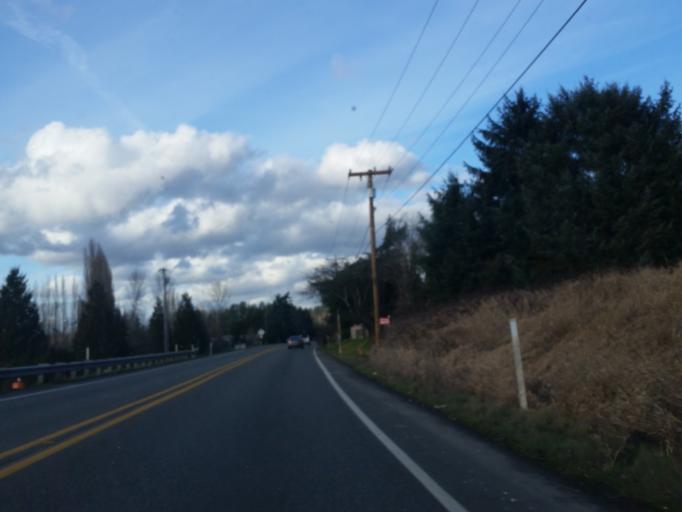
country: US
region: Washington
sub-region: King County
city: Redmond
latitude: 47.7159
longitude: -122.1336
